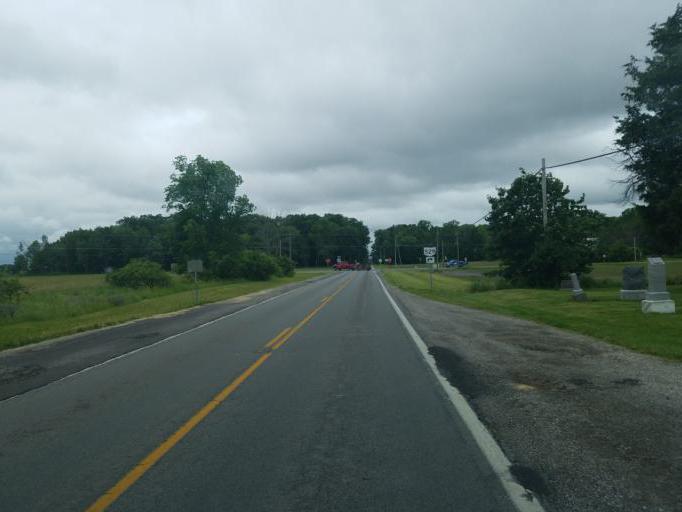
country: US
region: Ohio
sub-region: Marion County
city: Marion
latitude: 40.5495
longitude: -83.0773
